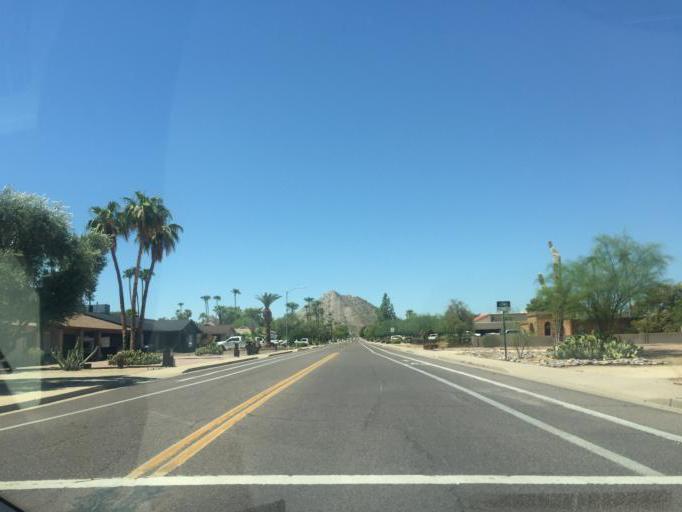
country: US
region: Arizona
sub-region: Maricopa County
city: Paradise Valley
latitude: 33.5896
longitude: -112.0218
